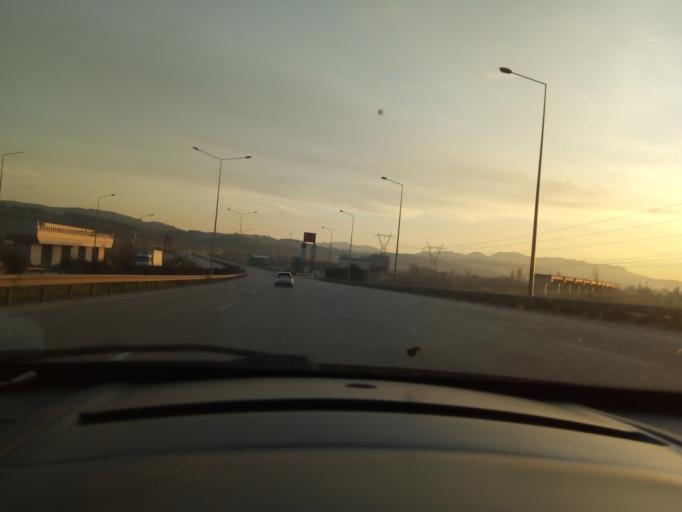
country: TR
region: Bursa
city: Niluefer
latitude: 40.2798
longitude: 28.9912
